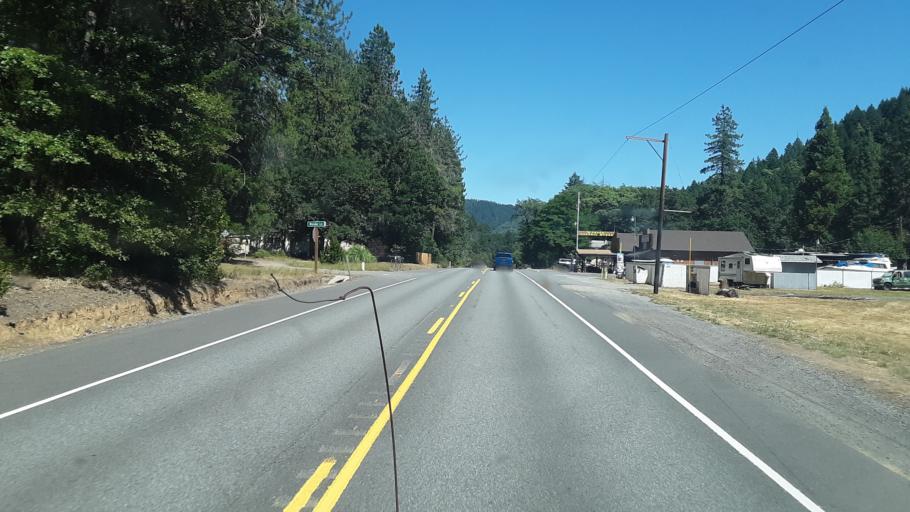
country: US
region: Oregon
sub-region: Josephine County
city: Redwood
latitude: 42.3637
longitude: -123.5314
